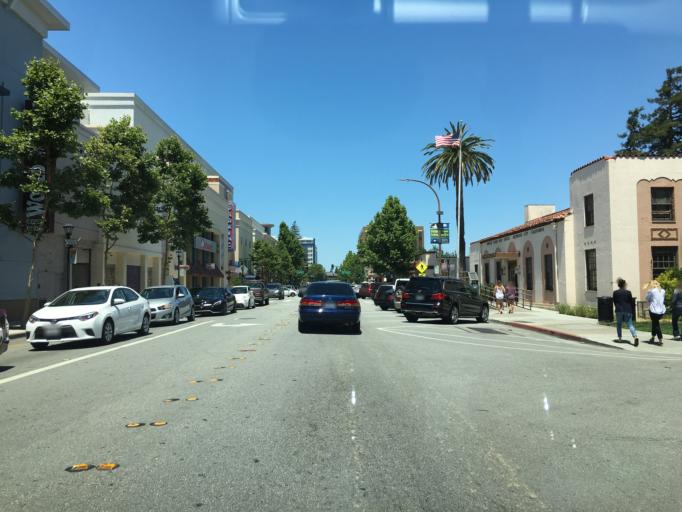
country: US
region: California
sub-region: San Mateo County
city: Redwood City
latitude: 37.4851
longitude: -122.2281
